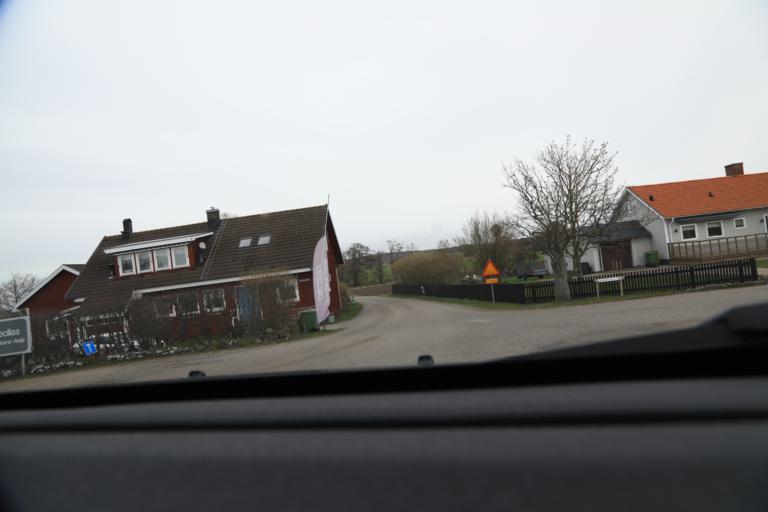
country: SE
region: Halland
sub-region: Varbergs Kommun
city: Traslovslage
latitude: 57.0700
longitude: 12.2904
